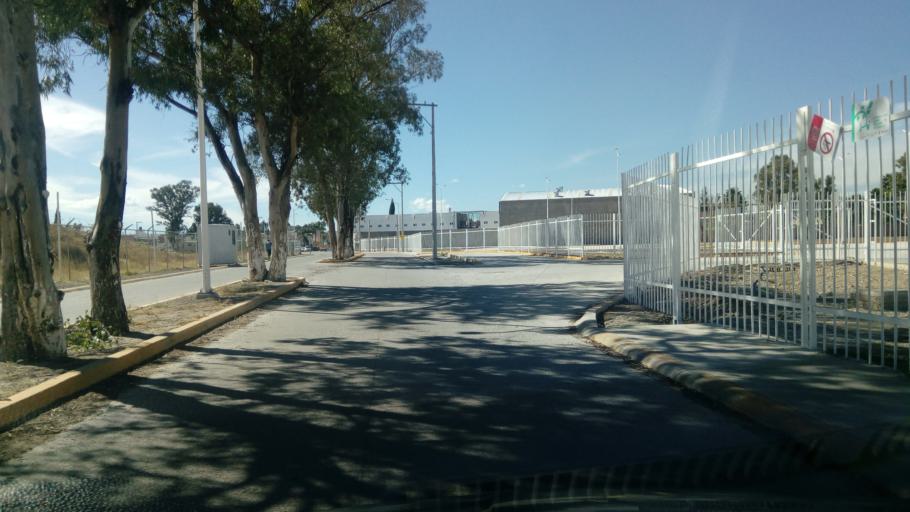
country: MX
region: Durango
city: Victoria de Durango
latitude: 24.0464
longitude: -104.6302
